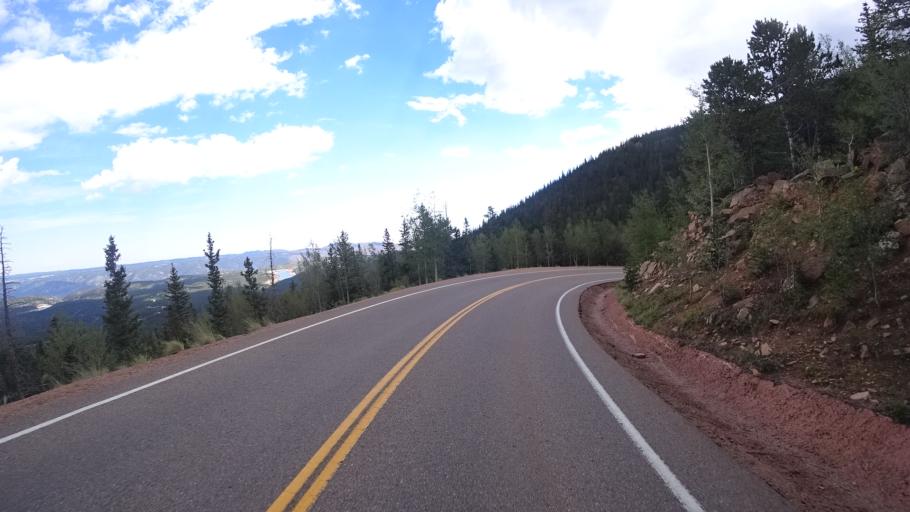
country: US
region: Colorado
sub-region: El Paso County
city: Cascade-Chipita Park
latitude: 38.8937
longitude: -105.0679
